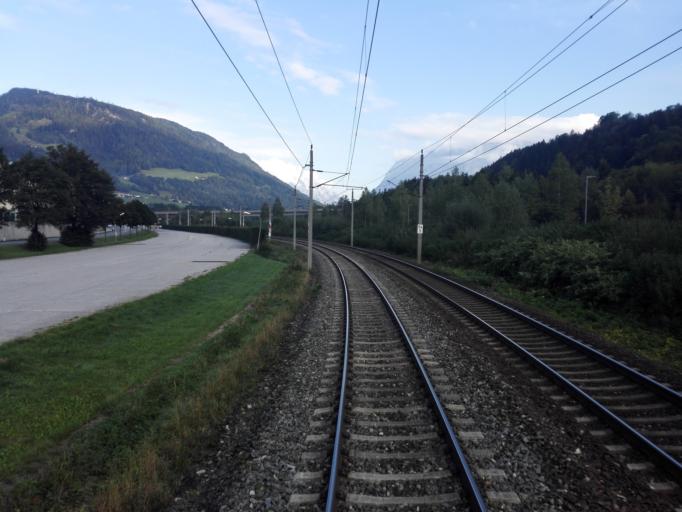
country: AT
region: Salzburg
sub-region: Politischer Bezirk Sankt Johann im Pongau
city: Bischofshofen
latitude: 47.4014
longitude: 13.2247
